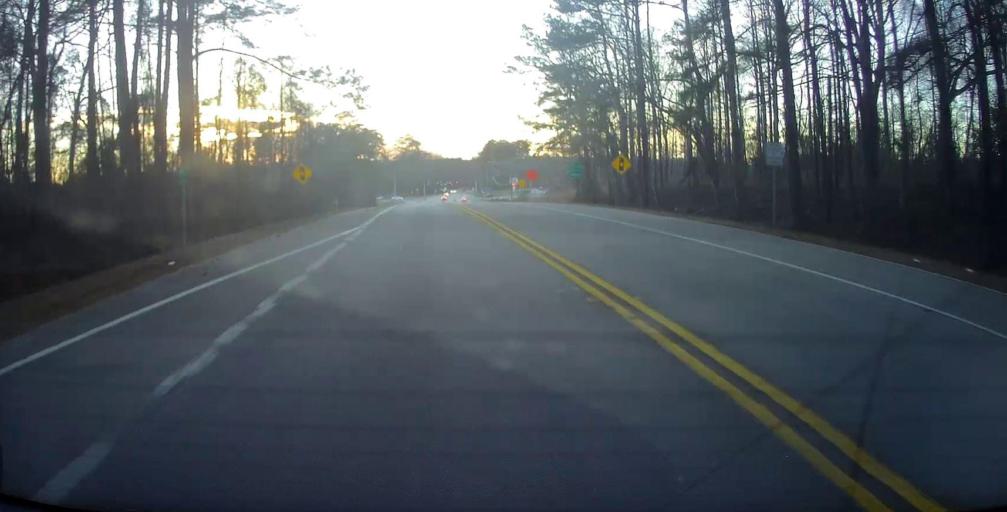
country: US
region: Georgia
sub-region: Troup County
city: La Grange
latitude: 33.0569
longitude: -84.9837
